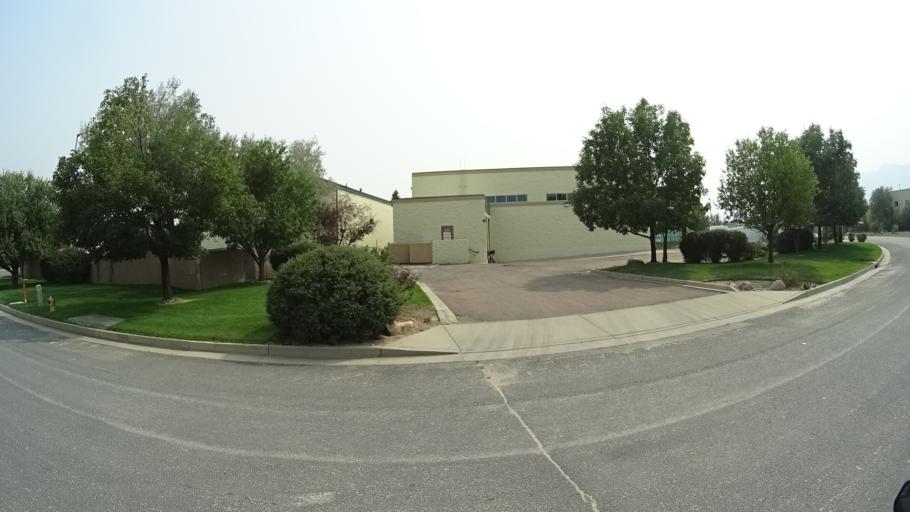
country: US
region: Colorado
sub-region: El Paso County
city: Stratmoor
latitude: 38.8012
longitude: -104.7962
